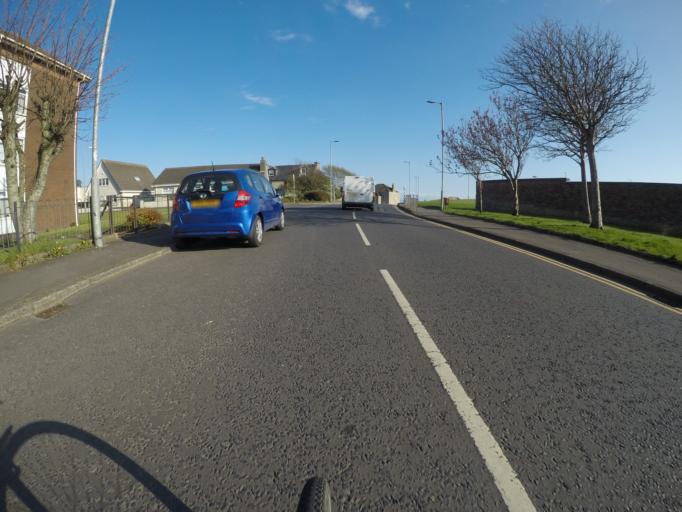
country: GB
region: Scotland
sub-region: North Ayrshire
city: Saltcoats
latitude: 55.6346
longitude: -4.7823
